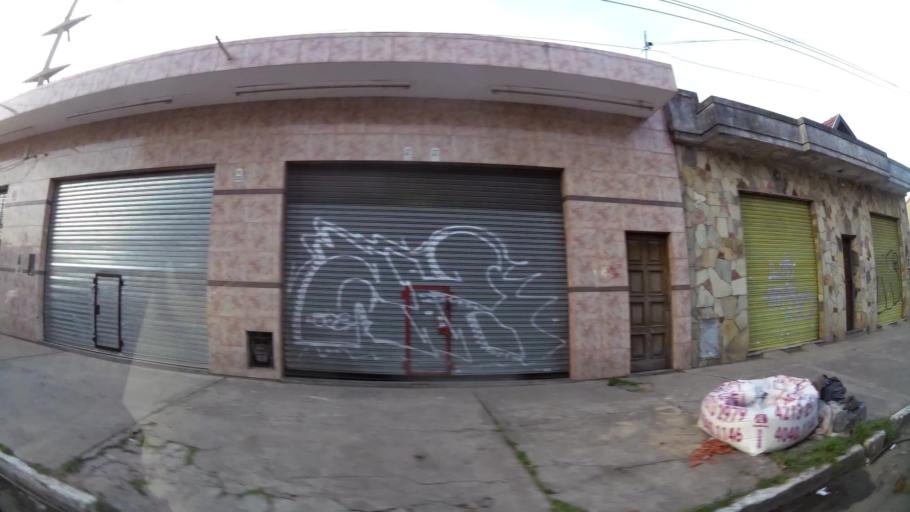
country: AR
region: Buenos Aires
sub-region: Partido de Almirante Brown
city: Adrogue
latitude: -34.7844
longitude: -58.3160
